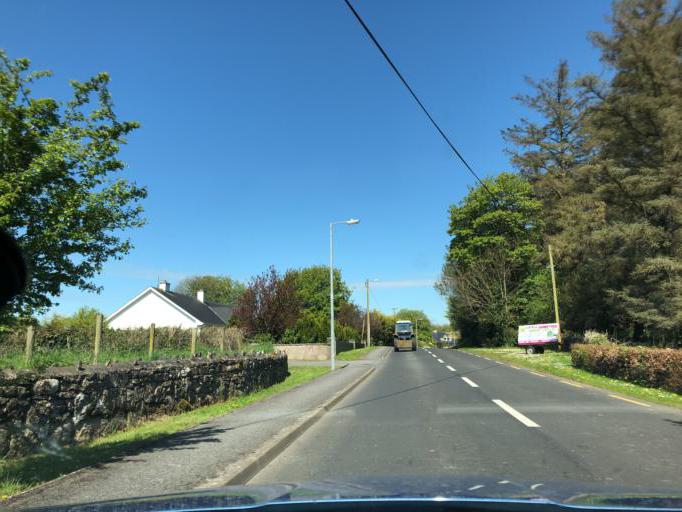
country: IE
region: Connaught
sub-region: County Galway
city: Portumna
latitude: 53.1457
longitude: -8.3703
